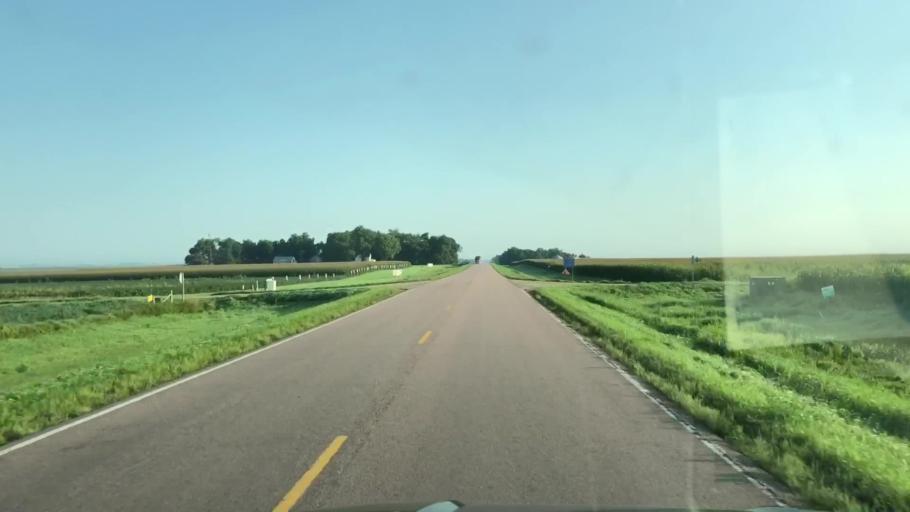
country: US
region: Iowa
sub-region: Lyon County
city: George
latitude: 43.2867
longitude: -95.9995
